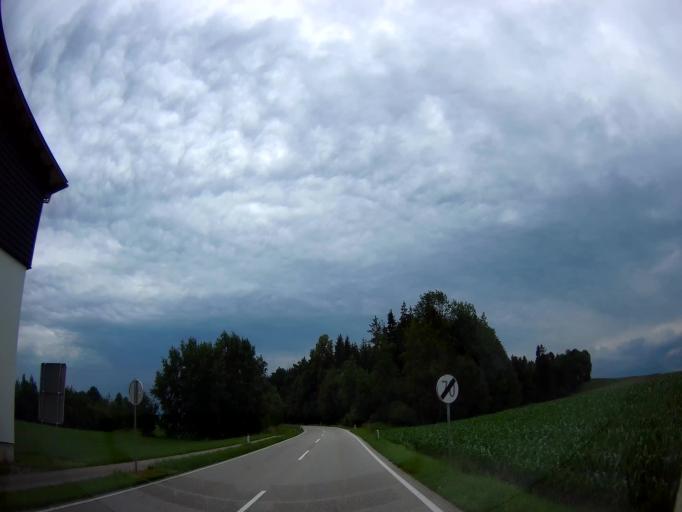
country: AT
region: Upper Austria
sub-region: Politischer Bezirk Braunau am Inn
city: Altheim
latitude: 48.2180
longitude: 13.1634
